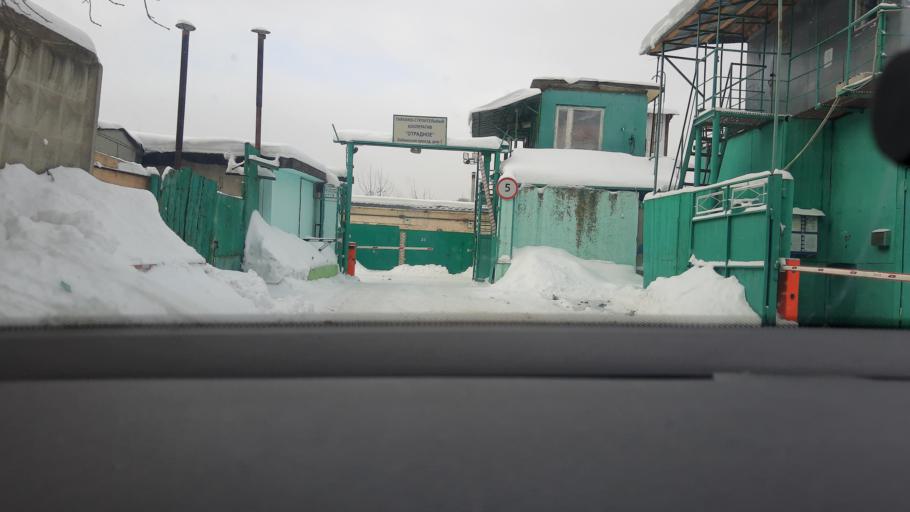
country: RU
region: Moscow
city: Rostokino
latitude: 55.8561
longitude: 37.6783
